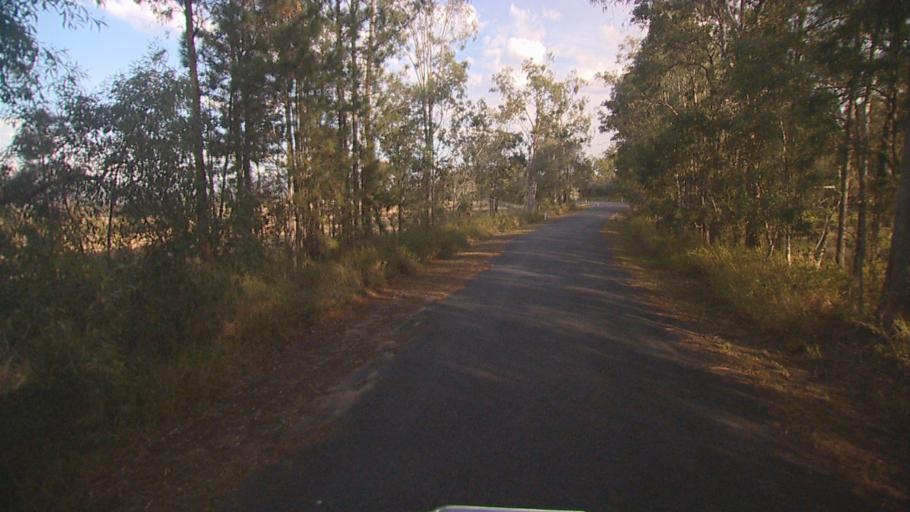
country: AU
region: Queensland
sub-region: Logan
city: Cedar Vale
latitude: -27.8429
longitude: 153.1194
